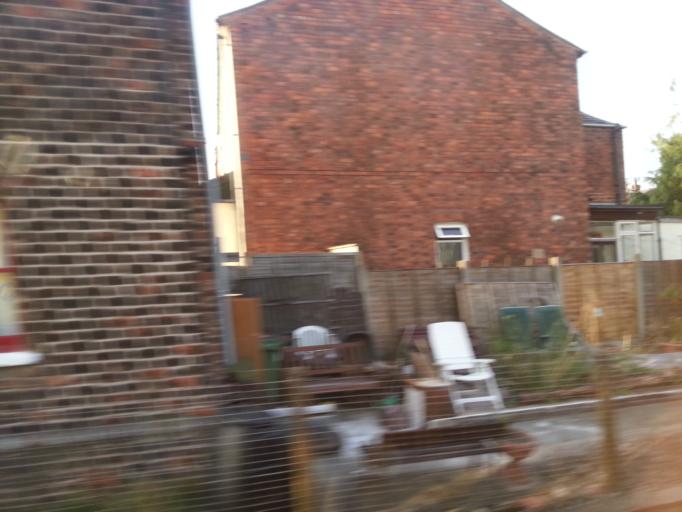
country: GB
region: England
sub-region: Sefton
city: Southport
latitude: 53.6417
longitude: -3.0032
